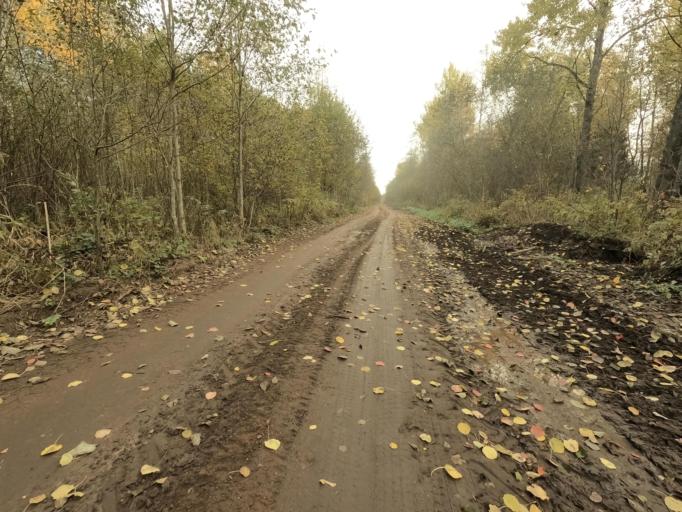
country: RU
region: Novgorod
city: Batetskiy
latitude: 58.8792
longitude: 30.7625
